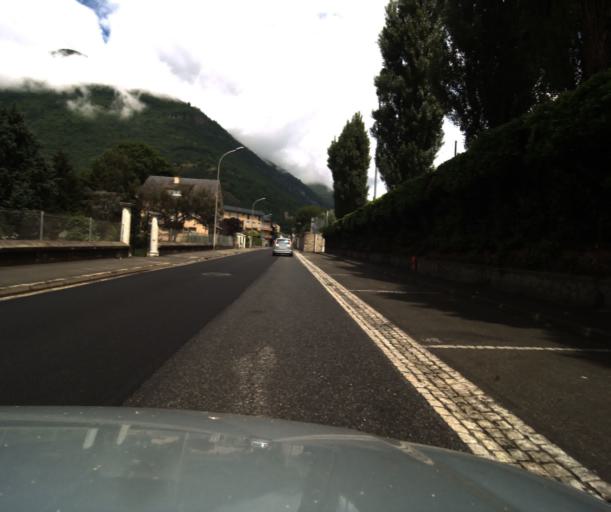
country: FR
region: Midi-Pyrenees
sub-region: Departement des Hautes-Pyrenees
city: Luz-Saint-Sauveur
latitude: 42.8714
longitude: -0.0064
